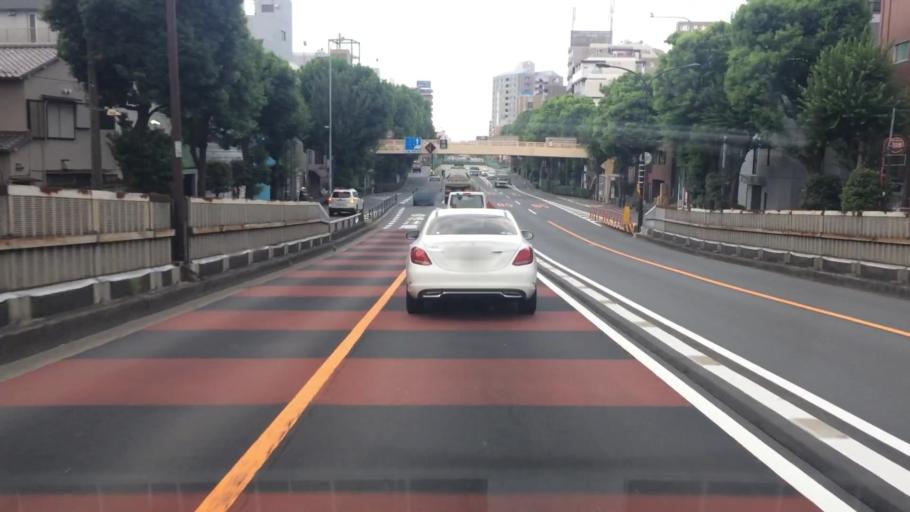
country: JP
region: Tokyo
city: Tokyo
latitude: 35.7221
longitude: 139.6538
